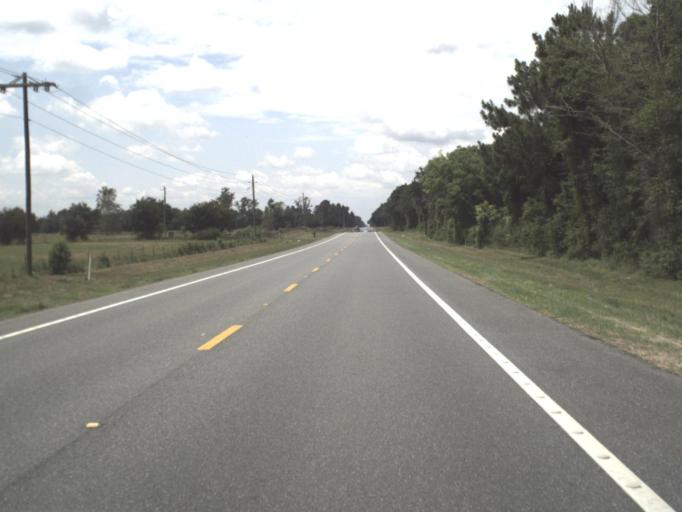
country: US
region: Florida
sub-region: Suwannee County
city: Wellborn
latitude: 30.1208
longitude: -82.9497
